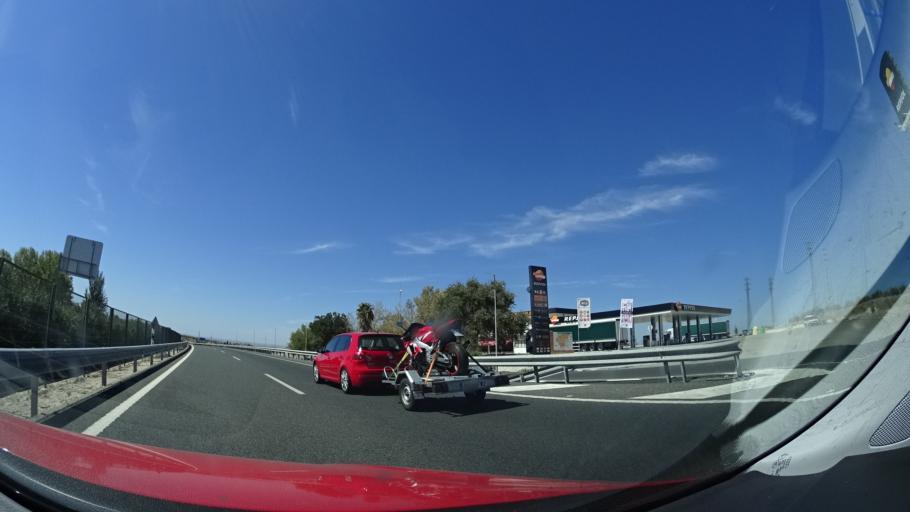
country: ES
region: Andalusia
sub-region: Provincia de Sevilla
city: Estepa
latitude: 37.3023
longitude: -4.8761
